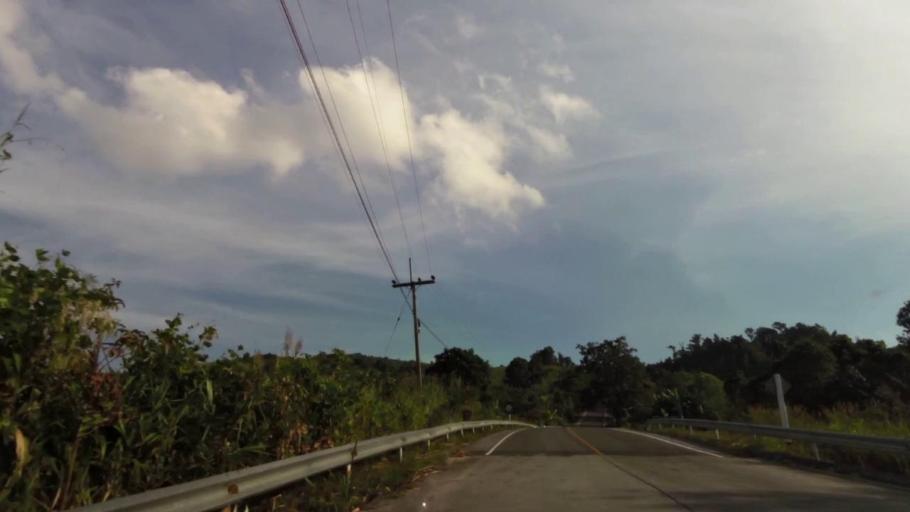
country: TH
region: Chiang Rai
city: Khun Tan
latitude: 19.8749
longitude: 100.3200
